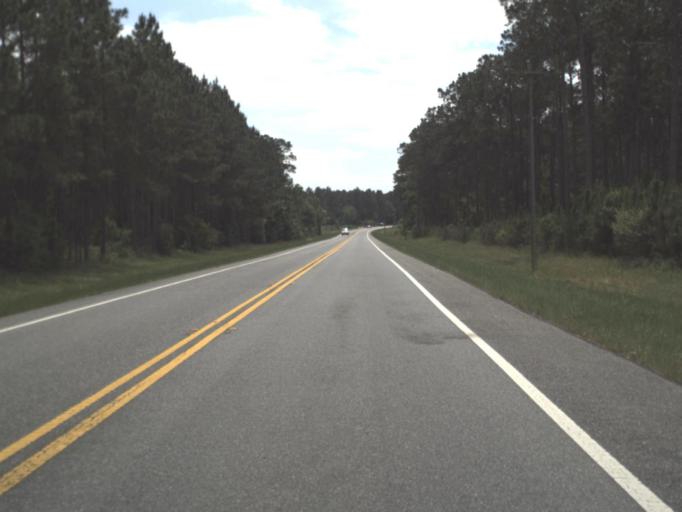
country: US
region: Florida
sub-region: Calhoun County
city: Blountstown
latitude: 30.3943
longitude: -85.0859
